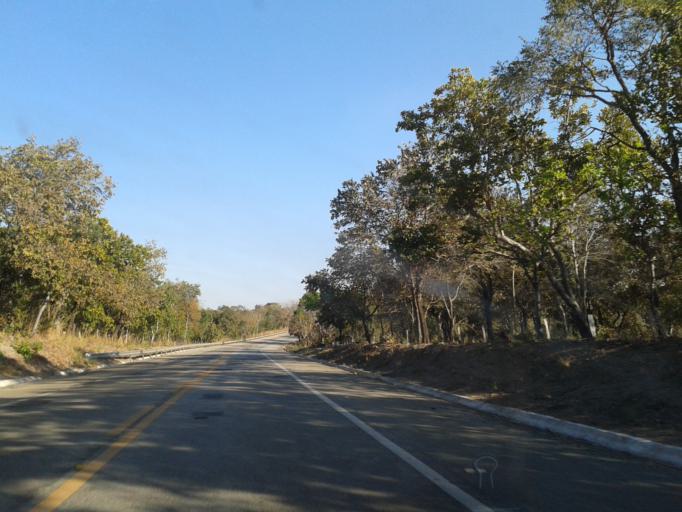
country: BR
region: Goias
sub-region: Itapirapua
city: Itapirapua
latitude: -15.3277
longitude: -50.4272
